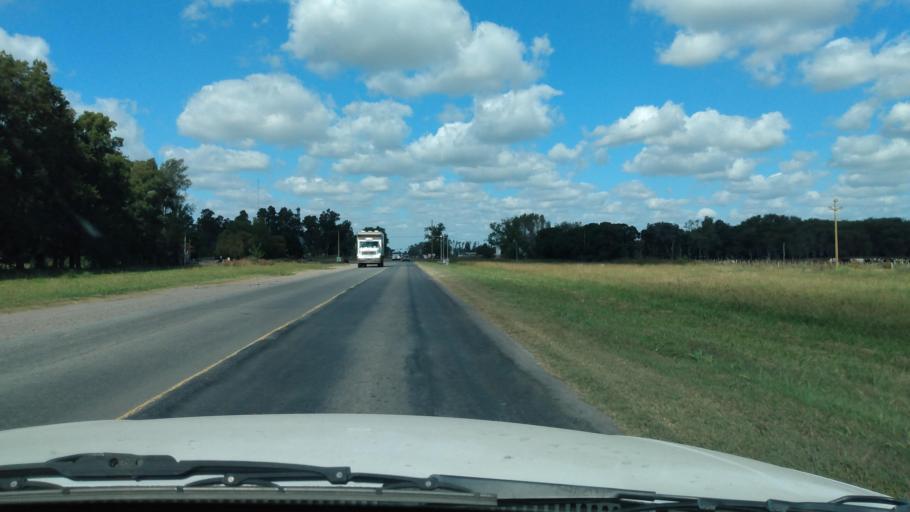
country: AR
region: Buenos Aires
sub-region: Partido de Navarro
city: Navarro
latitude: -34.9924
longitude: -59.3149
